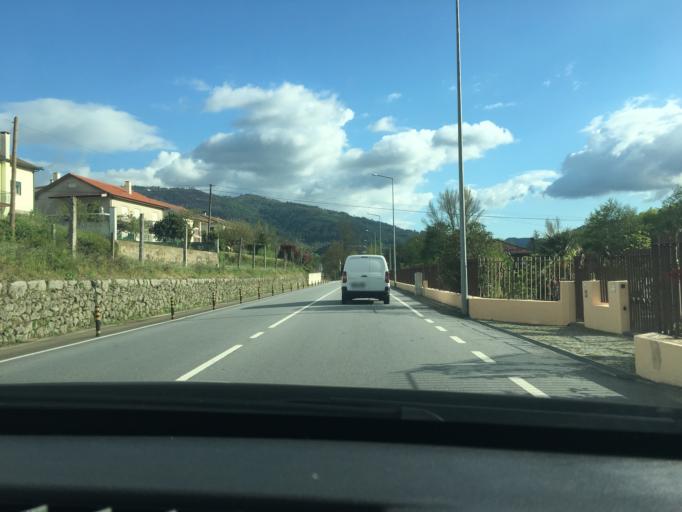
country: PT
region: Viana do Castelo
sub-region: Ponte da Barca
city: Ponte da Barca
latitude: 41.7954
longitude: -8.4144
